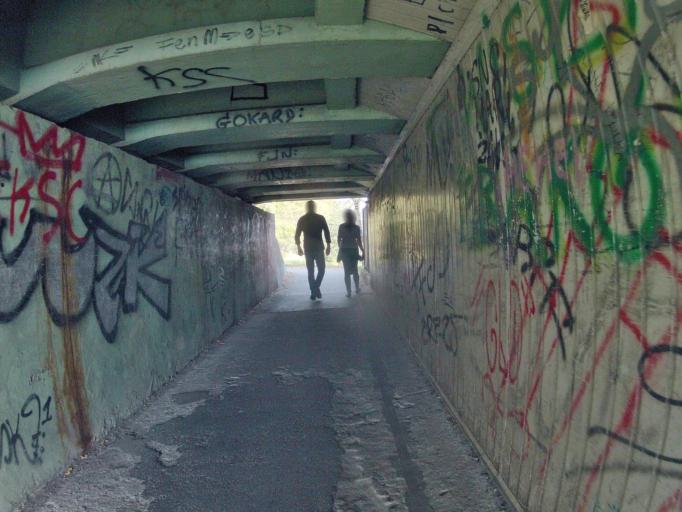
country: PL
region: Lesser Poland Voivodeship
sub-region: Krakow
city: Krakow
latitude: 50.0544
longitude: 19.9763
